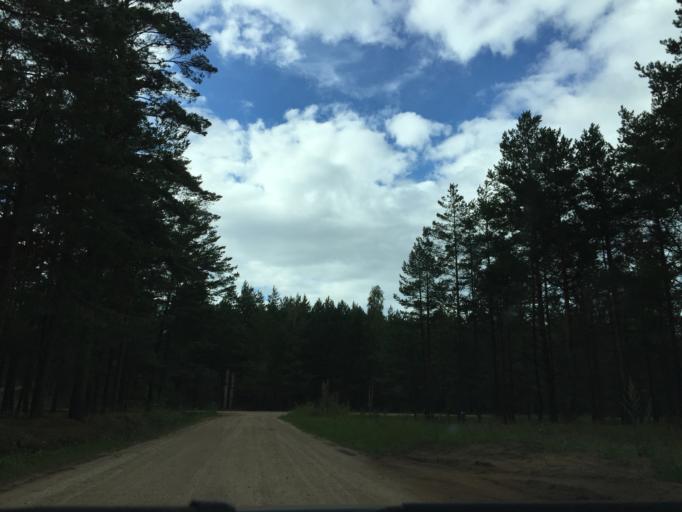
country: LV
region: Saulkrastu
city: Saulkrasti
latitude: 57.1726
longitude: 24.3805
